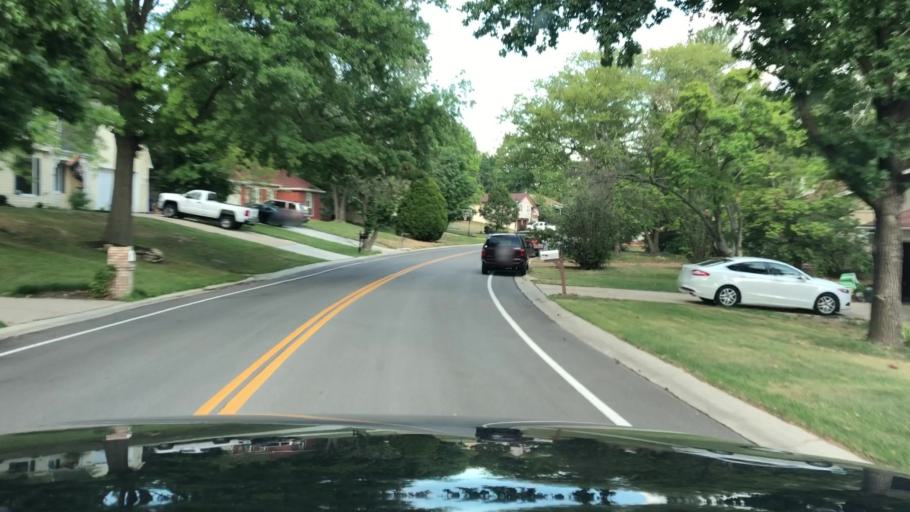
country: US
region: Missouri
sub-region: Saint Charles County
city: Lake Saint Louis
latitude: 38.7941
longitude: -90.8001
